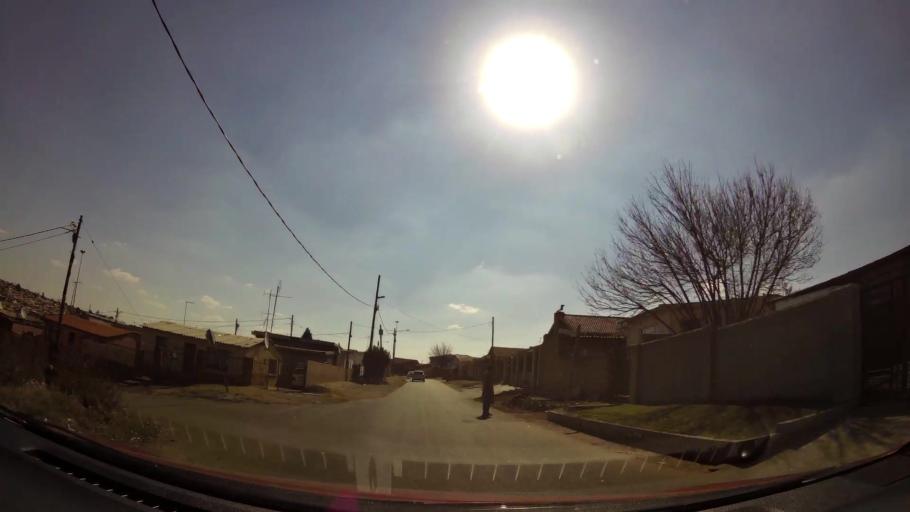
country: ZA
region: Gauteng
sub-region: City of Johannesburg Metropolitan Municipality
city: Soweto
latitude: -26.2307
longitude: 27.8894
